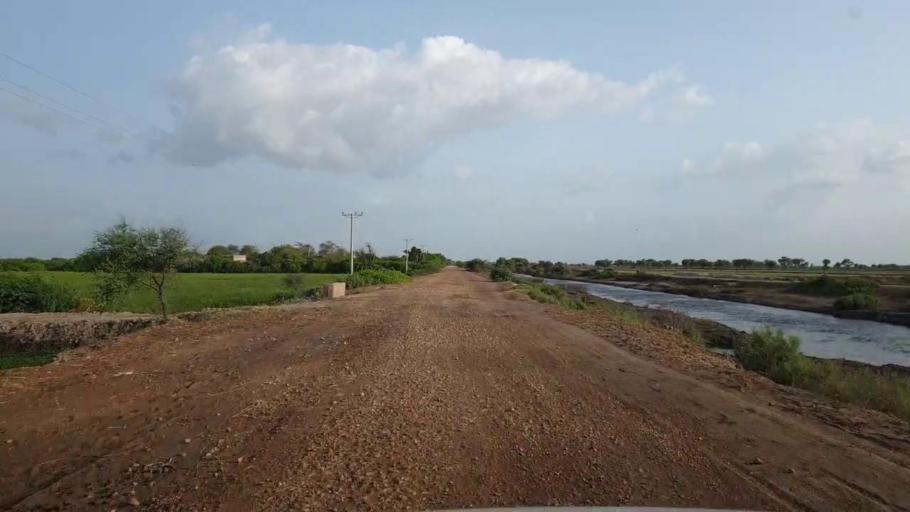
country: PK
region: Sindh
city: Kario
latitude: 24.8135
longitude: 68.6468
